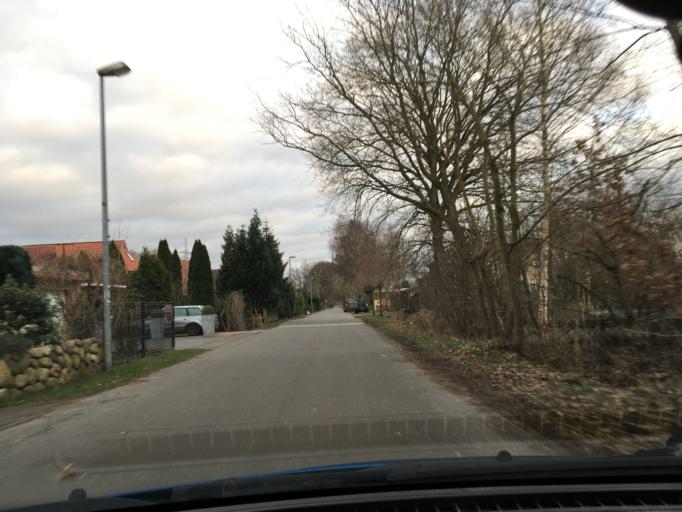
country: DE
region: Lower Saxony
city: Brietlingen
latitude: 53.3134
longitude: 10.4457
